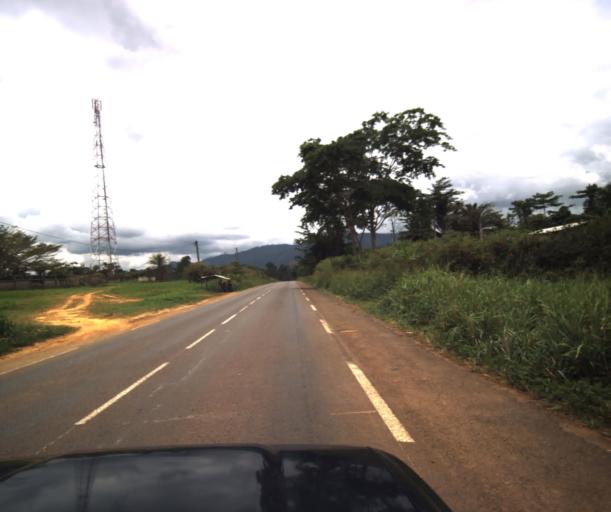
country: CM
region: Centre
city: Eseka
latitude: 3.8793
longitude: 10.8124
